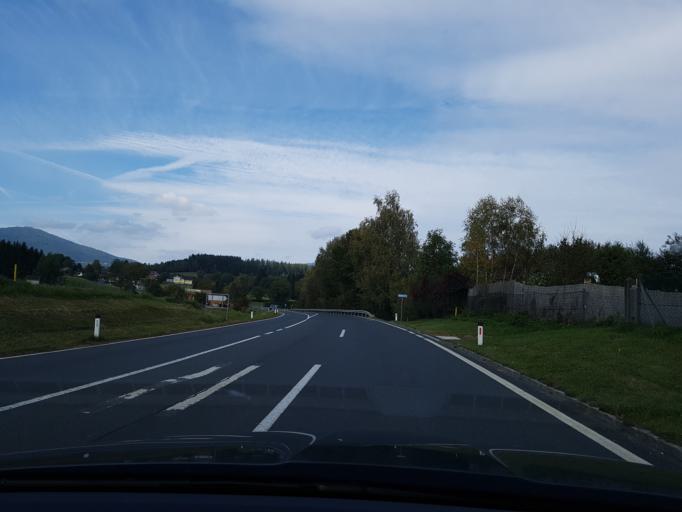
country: AT
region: Carinthia
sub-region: Politischer Bezirk Feldkirchen
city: Feldkirchen in Karnten
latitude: 46.7341
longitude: 14.0731
